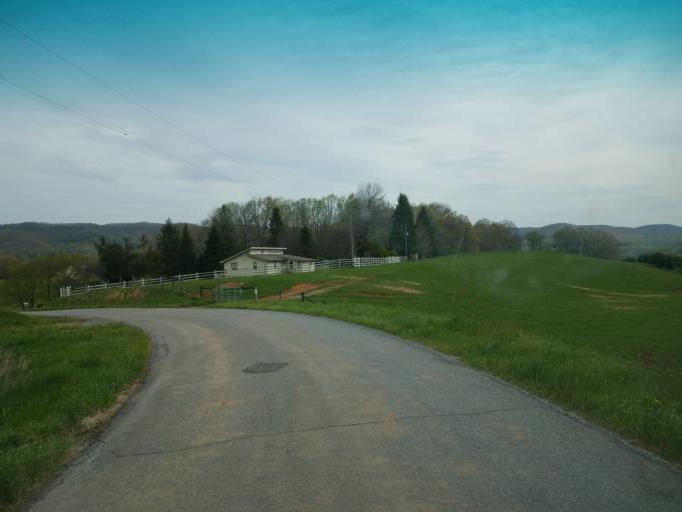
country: US
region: Virginia
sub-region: Smyth County
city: Marion
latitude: 36.7632
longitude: -81.4579
